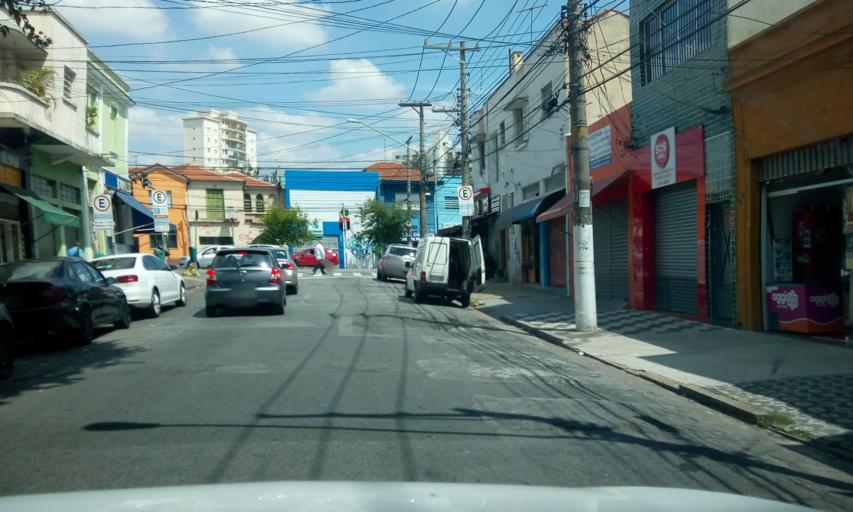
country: BR
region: Sao Paulo
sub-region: Sao Paulo
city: Sao Paulo
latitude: -23.5240
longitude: -46.7073
